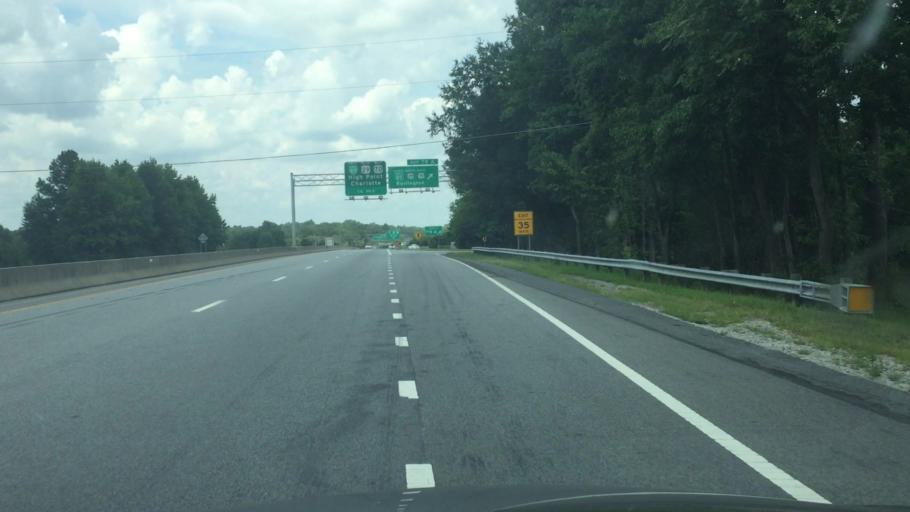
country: US
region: North Carolina
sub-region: Guilford County
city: Greensboro
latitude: 36.0155
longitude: -79.8261
